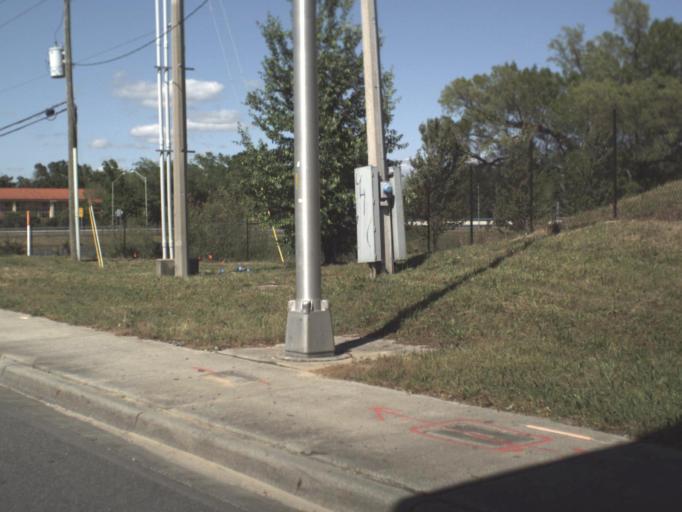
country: US
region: Florida
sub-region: Escambia County
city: Ferry Pass
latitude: 30.5039
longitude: -87.2214
